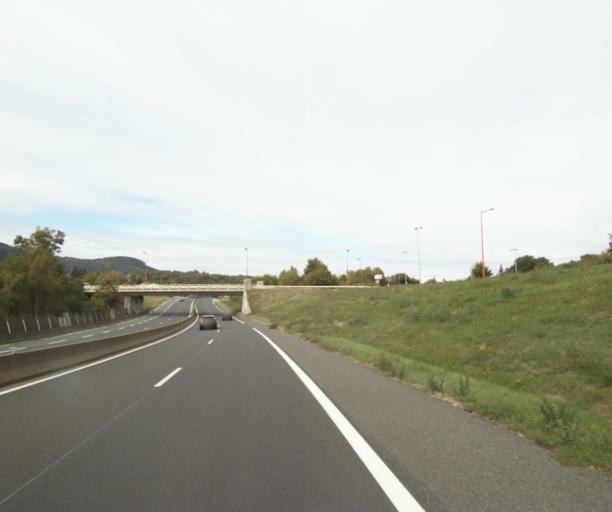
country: FR
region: Auvergne
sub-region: Departement du Puy-de-Dome
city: Ceyrat
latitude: 45.7300
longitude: 3.0699
